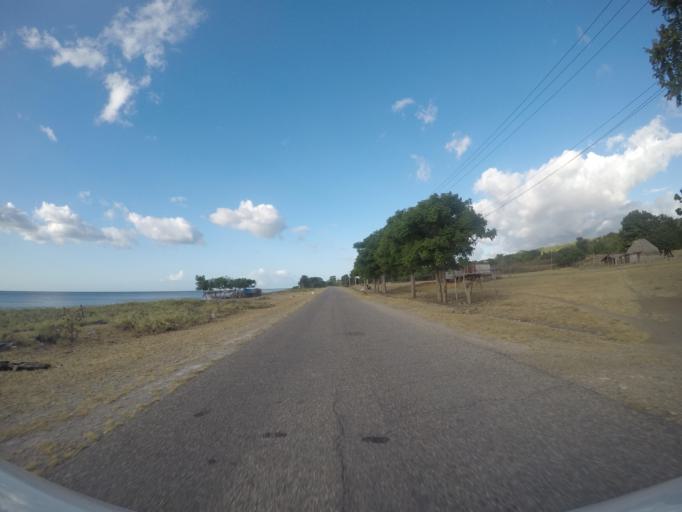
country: TL
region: Lautem
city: Lospalos
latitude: -8.3529
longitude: 126.9162
